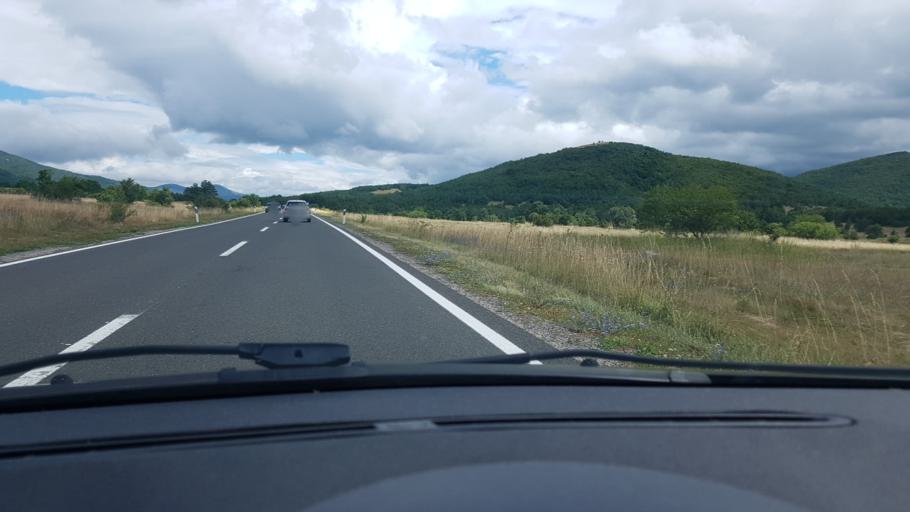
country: HR
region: Zadarska
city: Gracac
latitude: 44.4629
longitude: 15.8060
